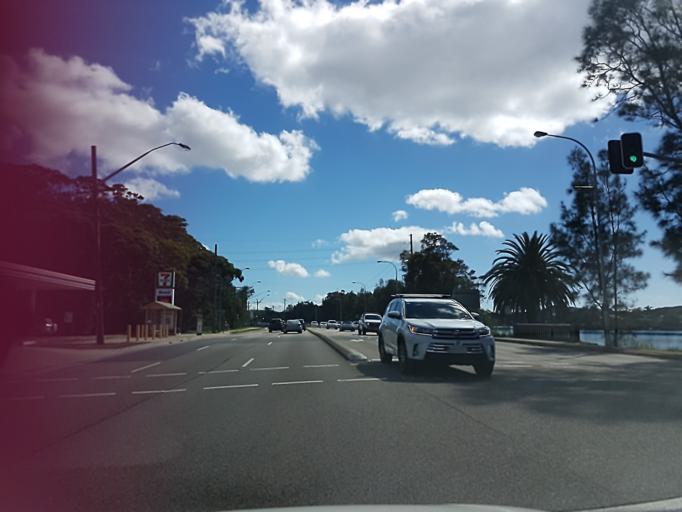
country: AU
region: New South Wales
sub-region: Pittwater
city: North Narrabeen
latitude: -33.7079
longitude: 151.2965
